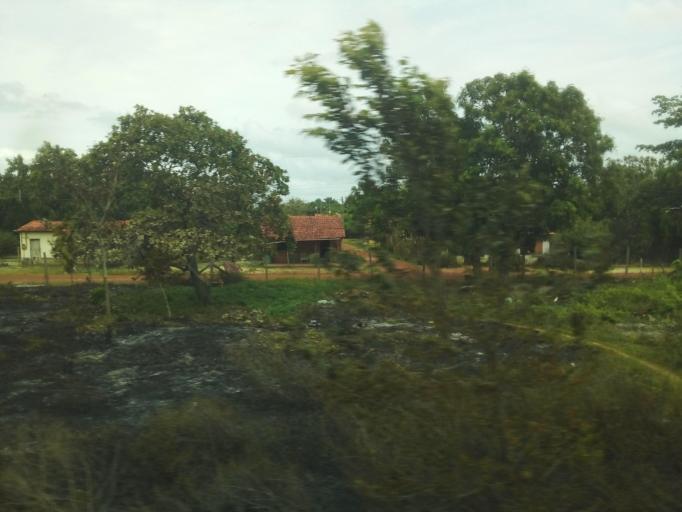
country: BR
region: Maranhao
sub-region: Itapecuru Mirim
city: Itapecuru Mirim
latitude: -3.3184
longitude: -44.4807
